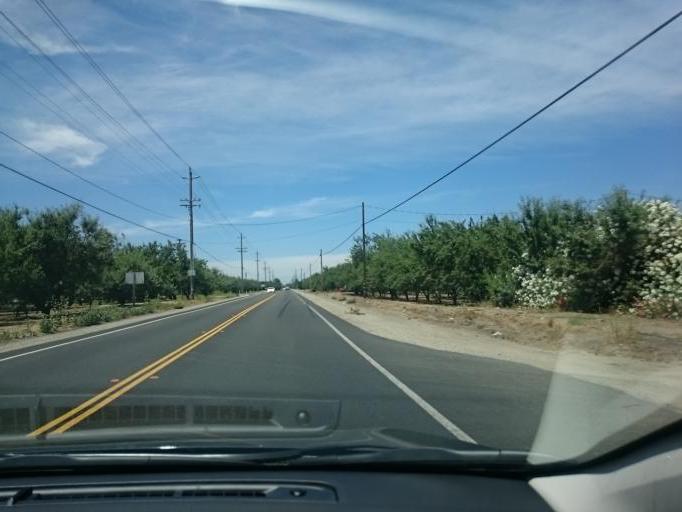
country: US
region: California
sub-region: Stanislaus County
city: Waterford
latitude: 37.6385
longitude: -120.7982
